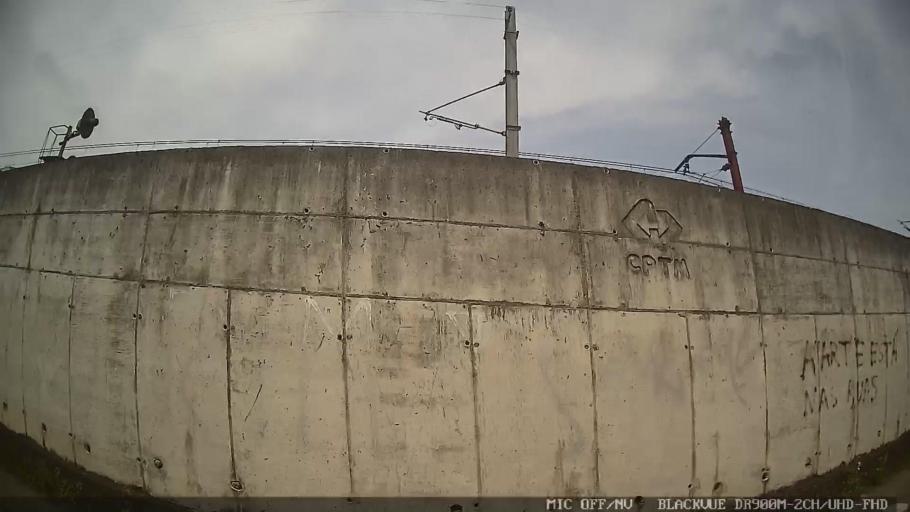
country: BR
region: Sao Paulo
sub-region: Itaquaquecetuba
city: Itaquaquecetuba
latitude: -23.4814
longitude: -46.3513
